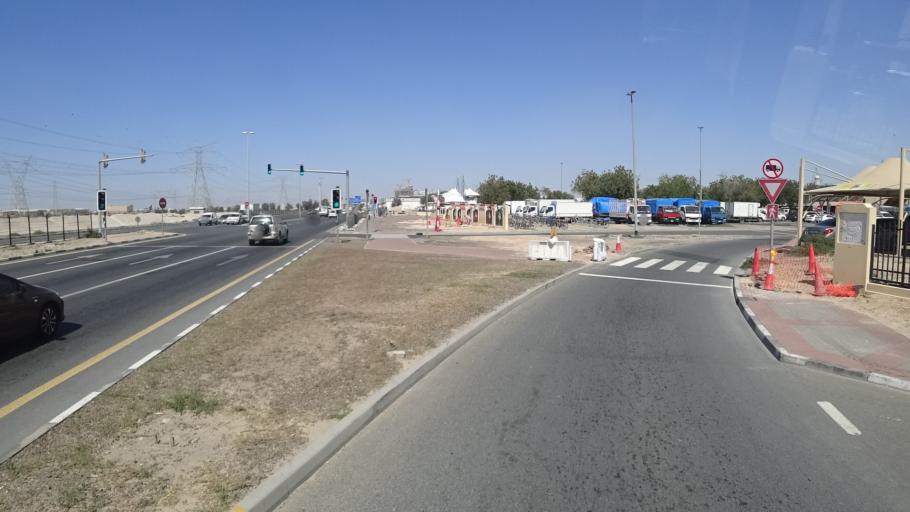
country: AE
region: Ash Shariqah
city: Sharjah
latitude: 25.1760
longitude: 55.3862
